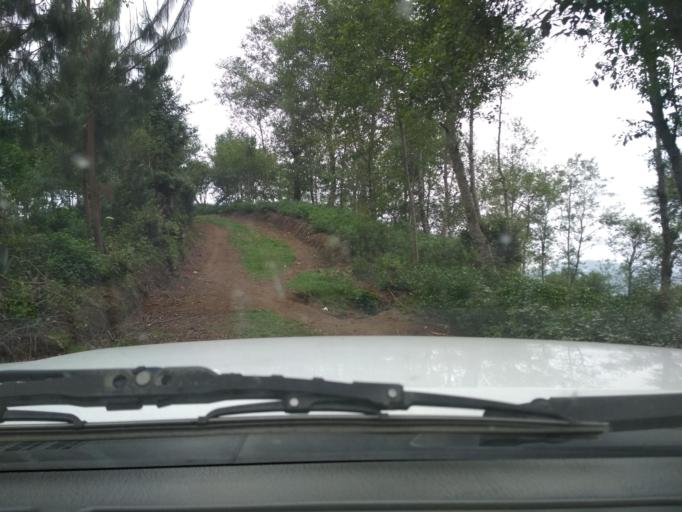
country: MX
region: Veracruz
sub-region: La Perla
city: Chilapa
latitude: 18.9899
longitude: -97.1661
